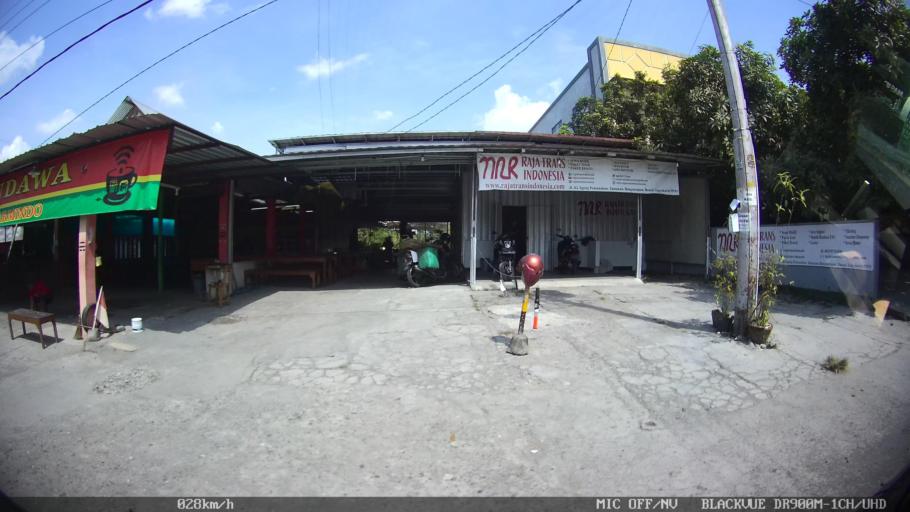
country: ID
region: Daerah Istimewa Yogyakarta
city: Sewon
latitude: -7.8316
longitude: 110.3806
